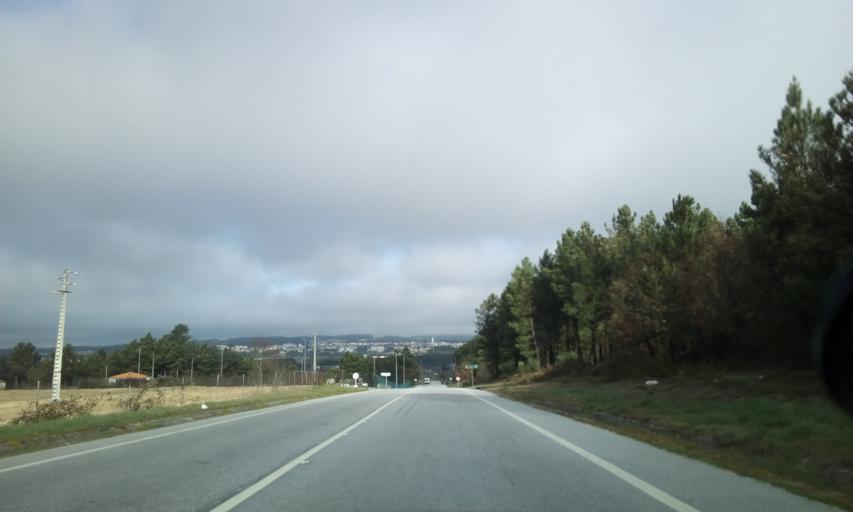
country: PT
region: Guarda
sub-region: Aguiar da Beira
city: Aguiar da Beira
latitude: 40.8023
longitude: -7.5228
